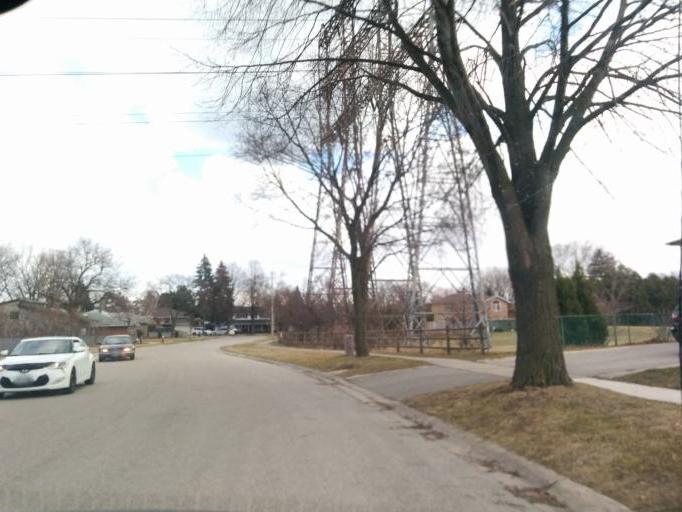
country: CA
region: Ontario
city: Etobicoke
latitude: 43.6077
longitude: -79.5674
